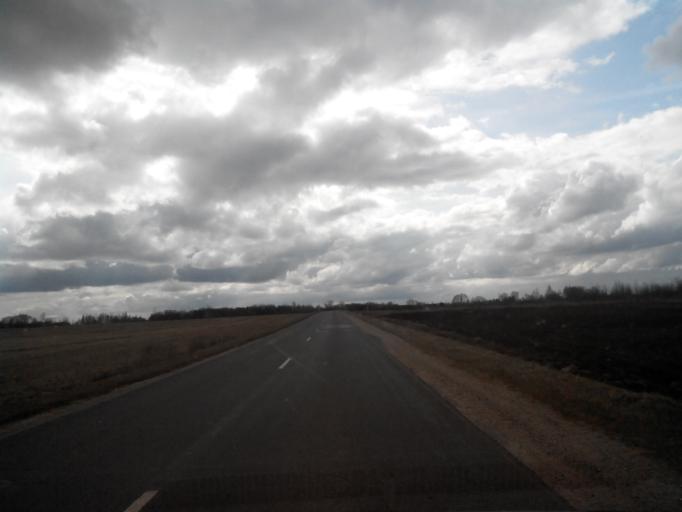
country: BY
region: Vitebsk
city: Pastavy
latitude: 55.1391
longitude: 26.9500
